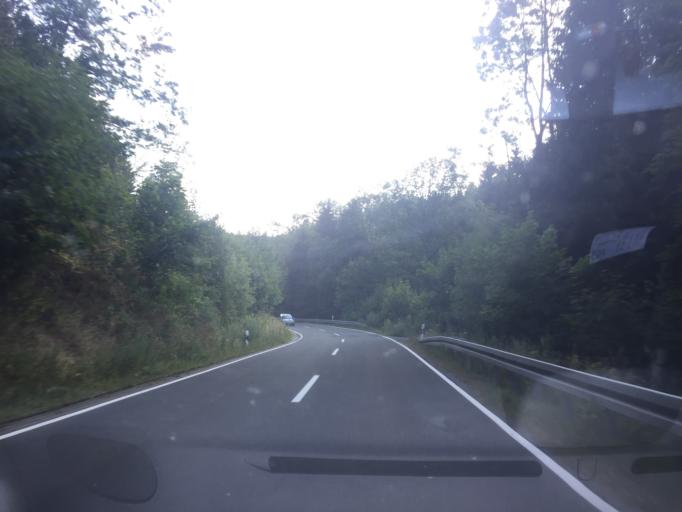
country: DE
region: Saxony-Anhalt
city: Darlingerode
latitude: 51.7974
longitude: 10.7352
